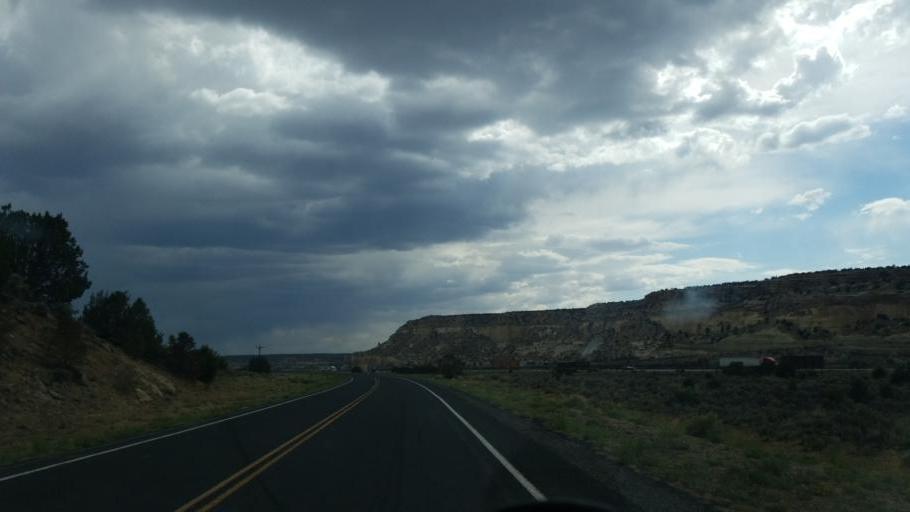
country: US
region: Arizona
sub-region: Apache County
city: Houck
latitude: 35.4121
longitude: -108.9939
